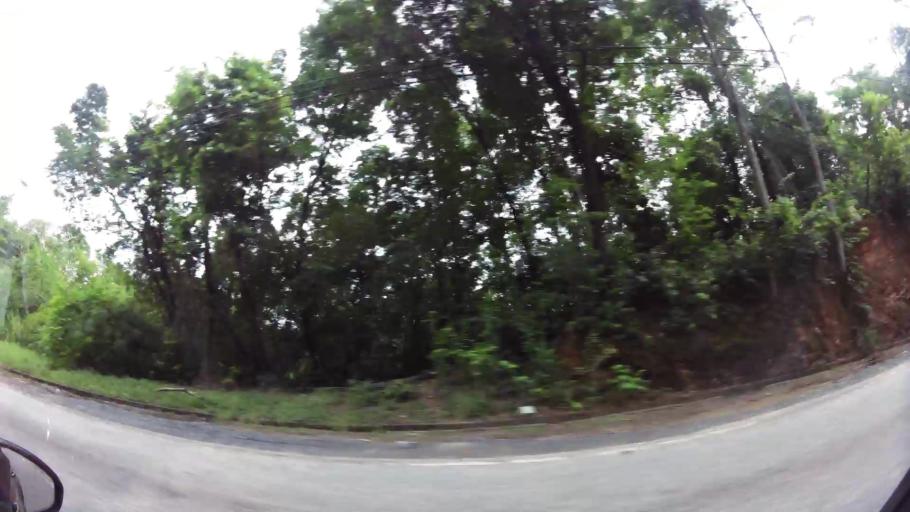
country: TT
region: City of Port of Spain
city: Port-of-Spain
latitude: 10.6725
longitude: -61.5054
